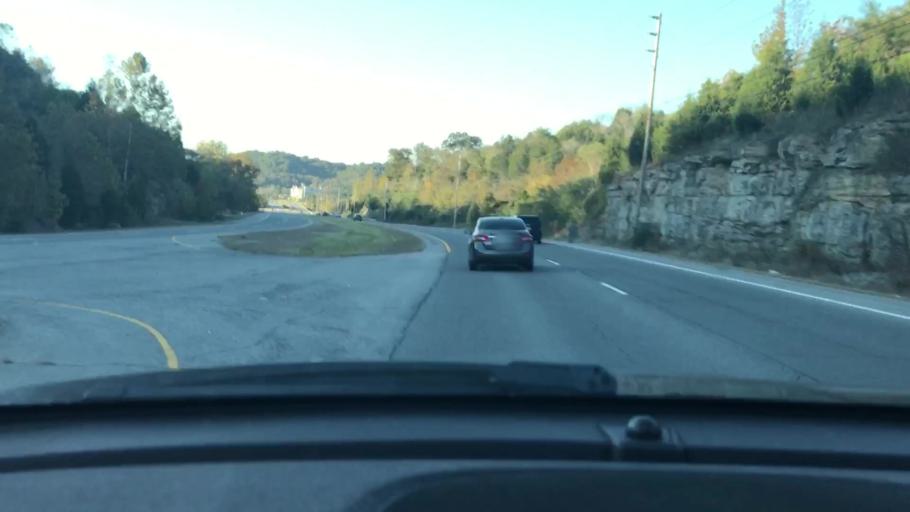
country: US
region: Tennessee
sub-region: Cheatham County
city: Ashland City
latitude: 36.2354
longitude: -87.0194
